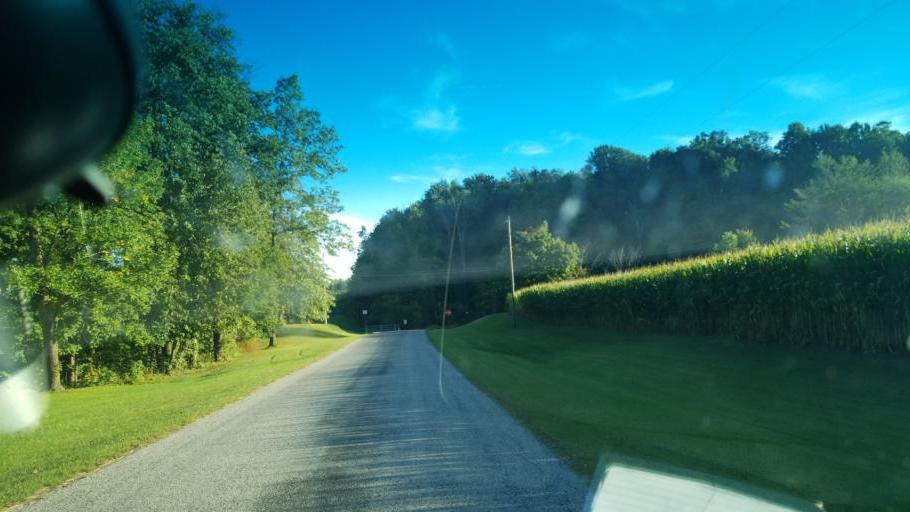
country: US
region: Ohio
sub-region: Crawford County
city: Galion
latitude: 40.6539
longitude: -82.7088
